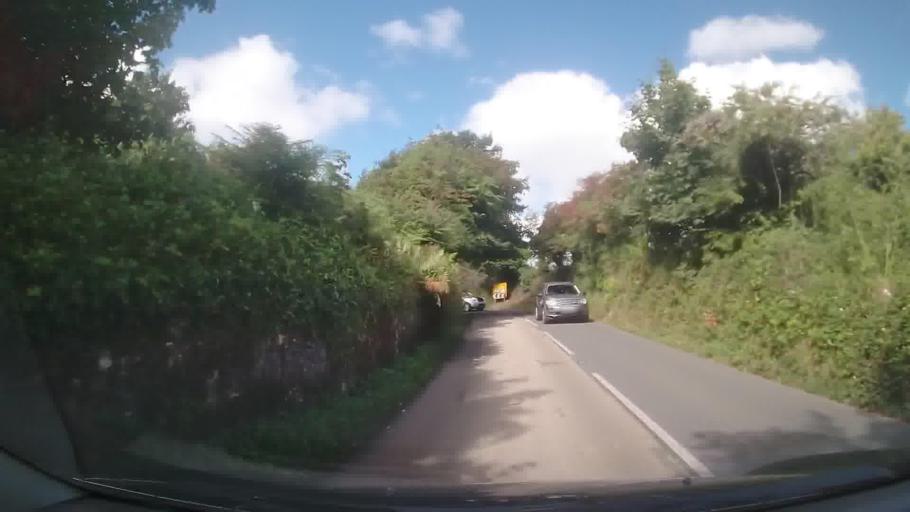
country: GB
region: Wales
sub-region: Pembrokeshire
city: Penally
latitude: 51.6569
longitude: -4.7428
